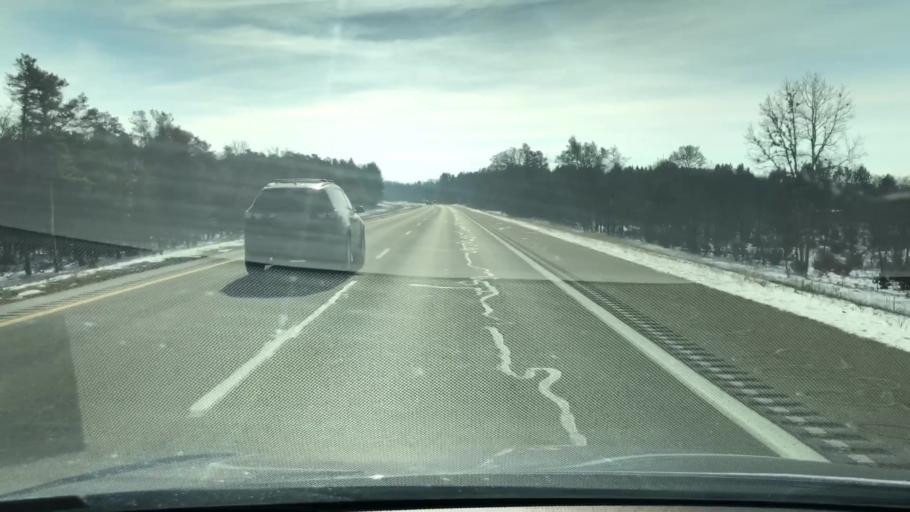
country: US
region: Michigan
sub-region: Crawford County
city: Grayling
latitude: 44.5644
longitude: -84.7059
